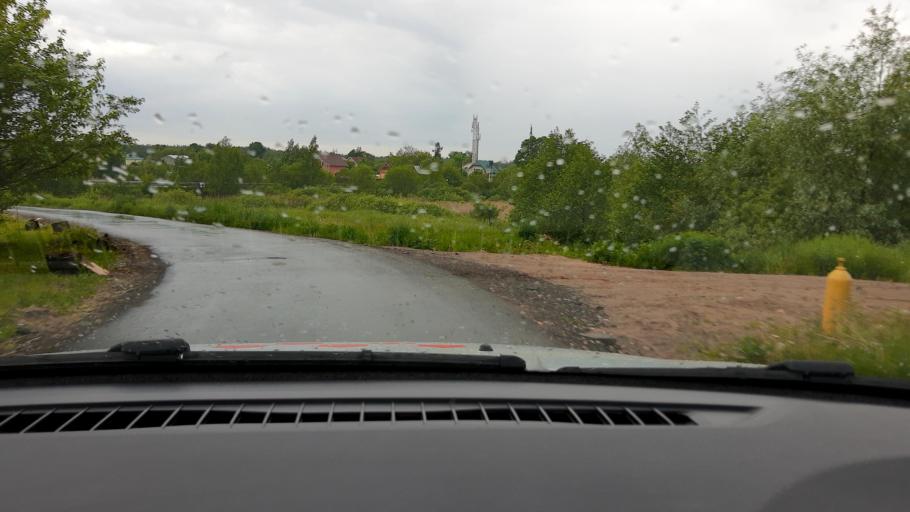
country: RU
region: Nizjnij Novgorod
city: Gorbatovka
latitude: 56.2317
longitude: 43.7234
